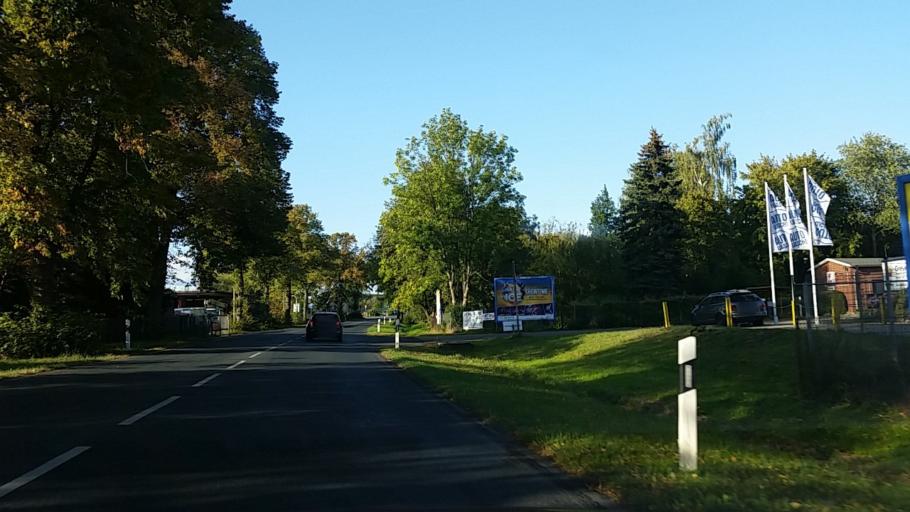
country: DE
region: Lower Saxony
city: Vordorf
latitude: 52.3325
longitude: 10.5211
